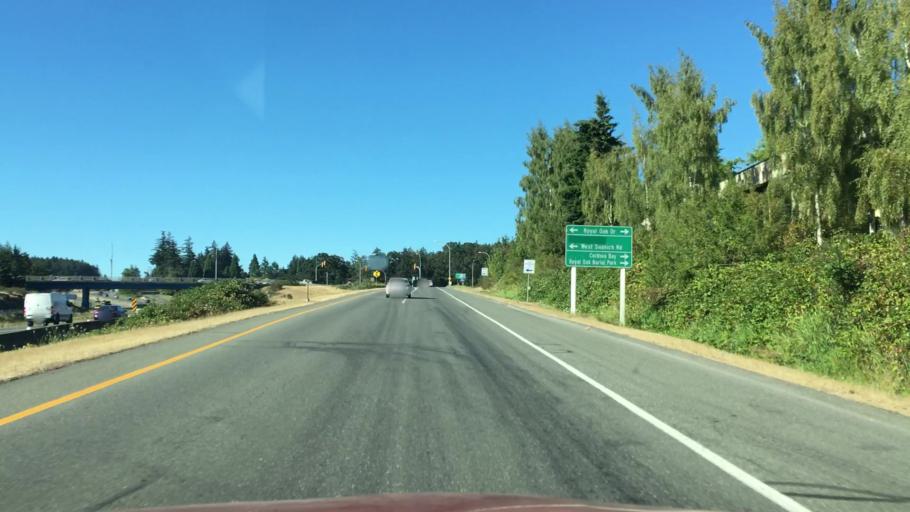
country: CA
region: British Columbia
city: Victoria
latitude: 48.4965
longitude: -123.3854
